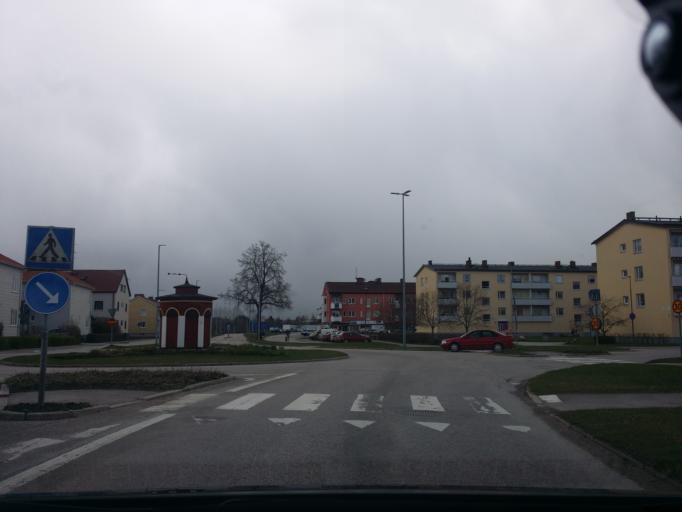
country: SE
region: Vaestmanland
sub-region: Sala Kommun
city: Sala
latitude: 59.9173
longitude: 16.6097
